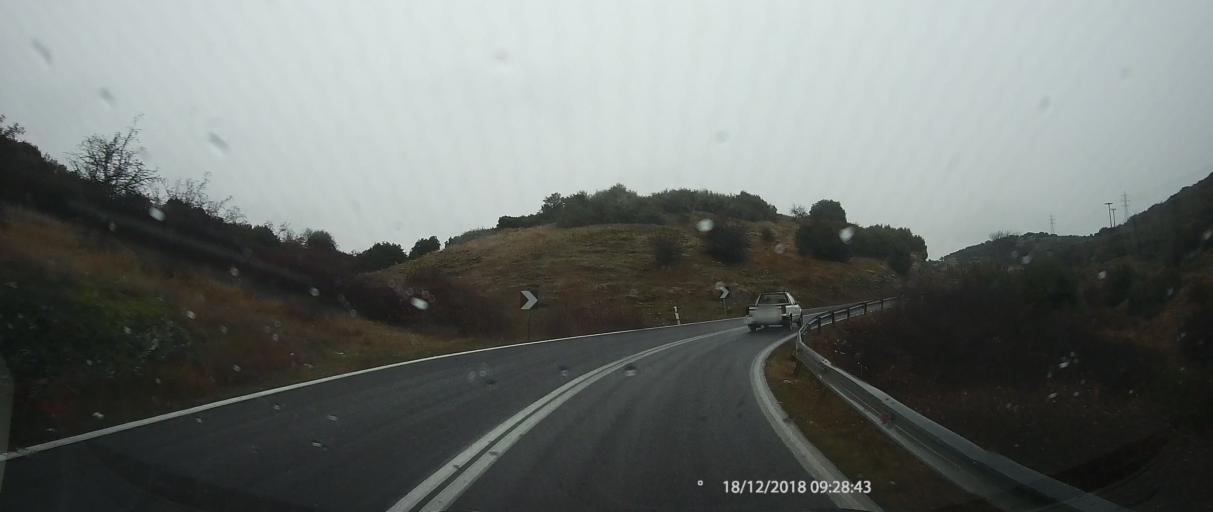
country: GR
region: Thessaly
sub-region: Nomos Larisis
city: Elassona
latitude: 39.9215
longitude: 22.1716
